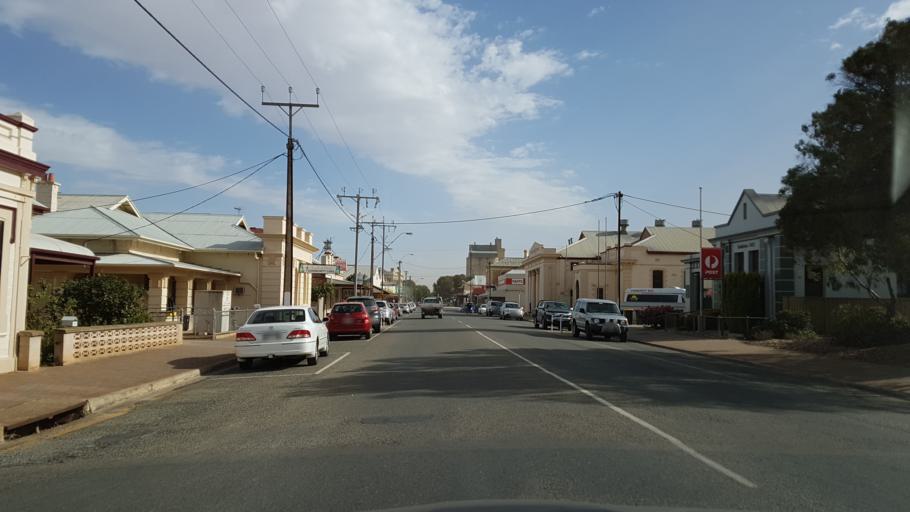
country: AU
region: South Australia
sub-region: Wakefield
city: Balaklava
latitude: -34.1474
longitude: 138.4156
